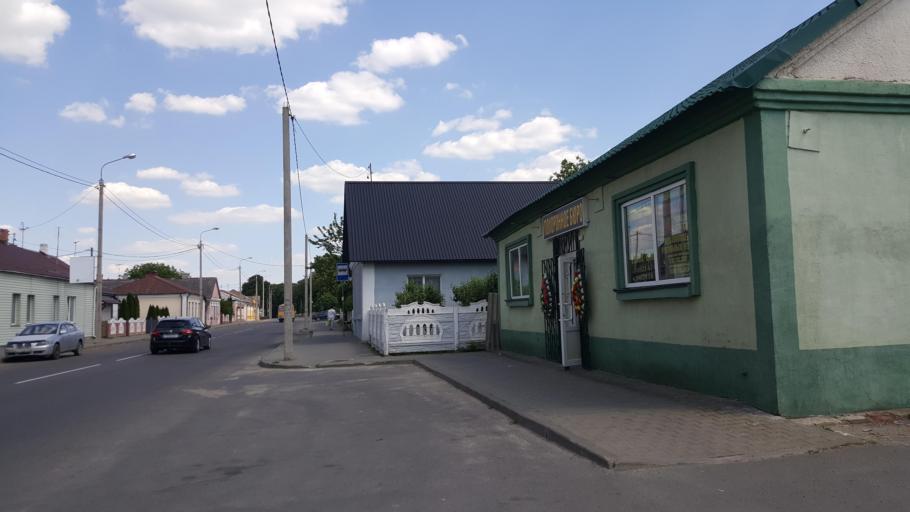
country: BY
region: Brest
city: Kobryn
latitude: 52.2123
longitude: 24.3619
